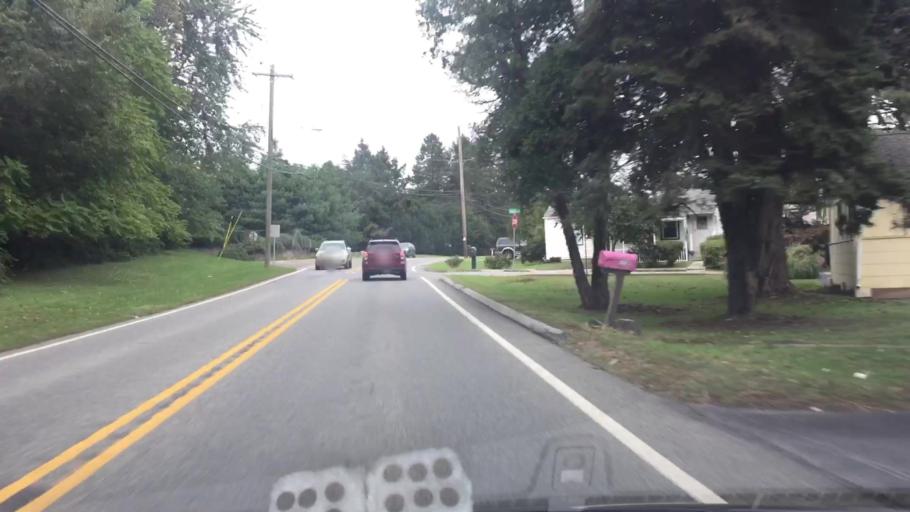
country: US
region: Pennsylvania
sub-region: Delaware County
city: Brookhaven
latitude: 39.8743
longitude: -75.4039
